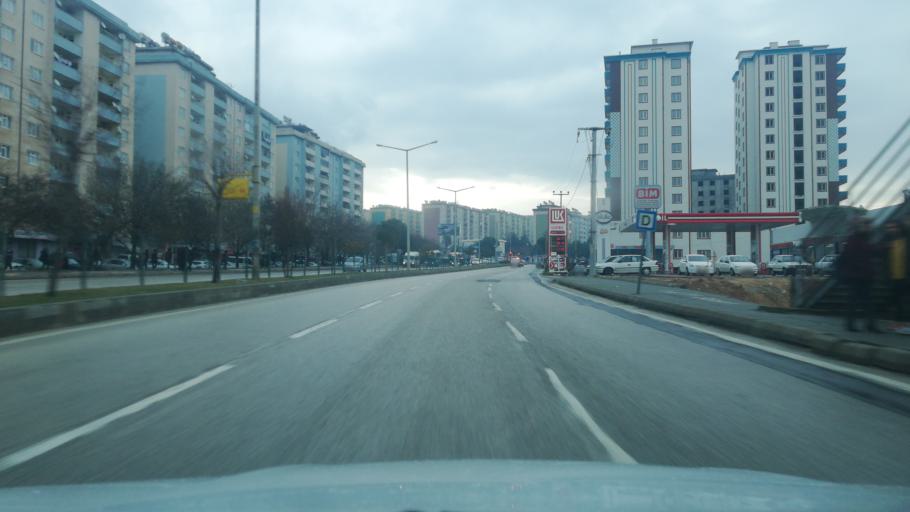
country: TR
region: Kahramanmaras
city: Kahramanmaras
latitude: 37.5831
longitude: 36.9790
